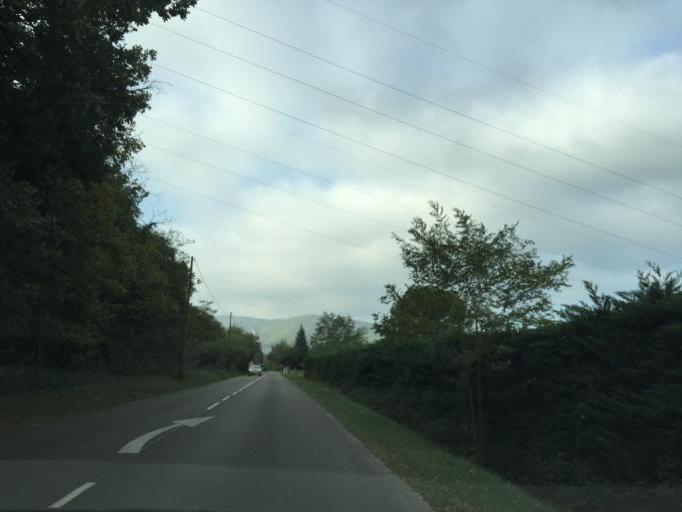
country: FR
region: Rhone-Alpes
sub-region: Departement de la Drome
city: Chateauneuf-du-Rhone
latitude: 44.4851
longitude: 4.7121
